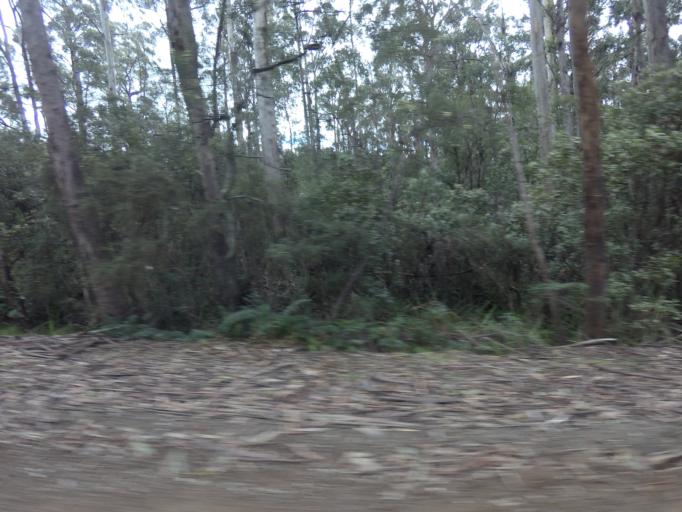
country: AU
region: Tasmania
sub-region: Huon Valley
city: Geeveston
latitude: -43.4238
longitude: 147.0081
